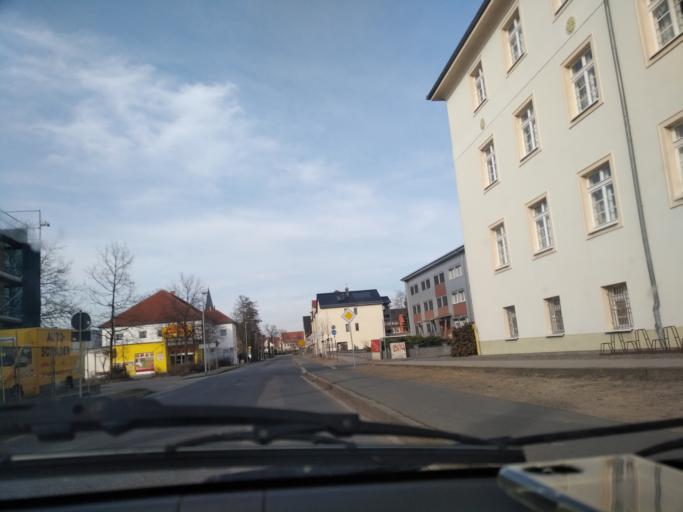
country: DE
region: Brandenburg
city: Bad Liebenwerda
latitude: 51.5123
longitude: 13.3927
